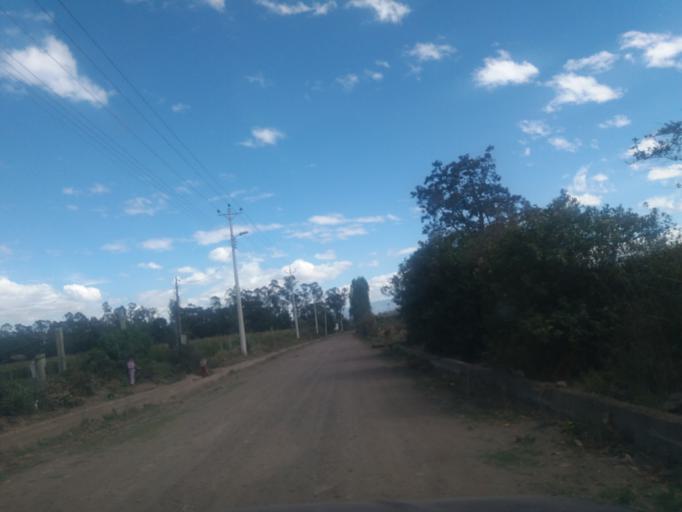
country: EC
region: Pichincha
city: Sangolqui
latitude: -0.1790
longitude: -78.3371
